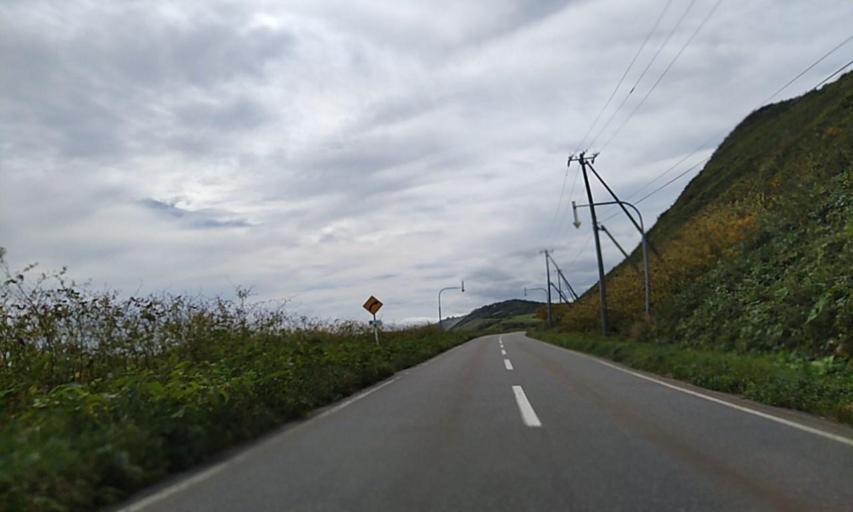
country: JP
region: Hokkaido
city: Obihiro
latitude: 42.7887
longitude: 143.7949
